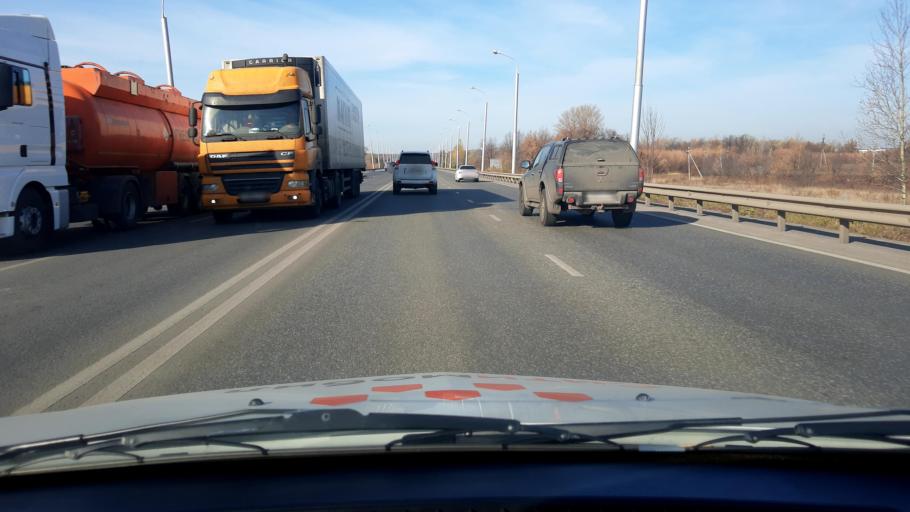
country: RU
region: Bashkortostan
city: Iglino
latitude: 54.8002
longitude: 56.1988
